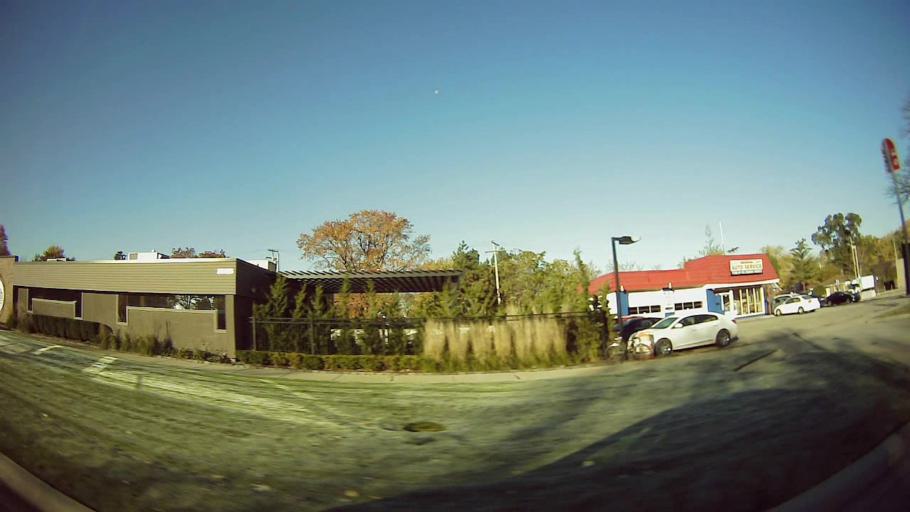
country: US
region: Michigan
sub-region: Oakland County
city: Huntington Woods
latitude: 42.4795
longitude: -83.1829
